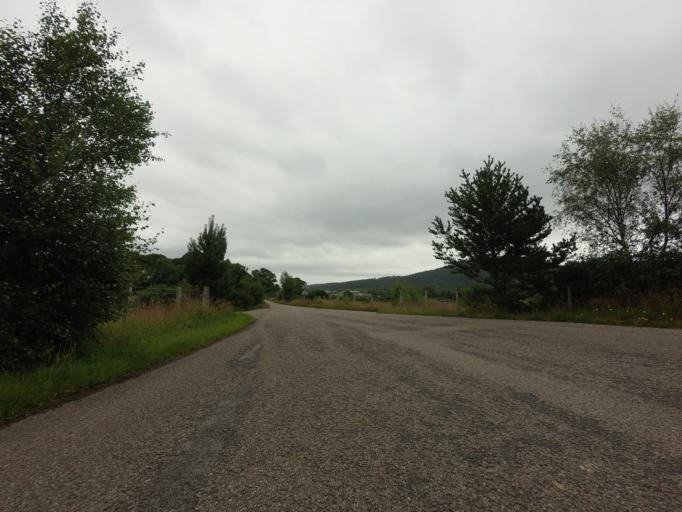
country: GB
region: Scotland
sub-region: Highland
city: Evanton
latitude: 57.9107
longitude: -4.3978
